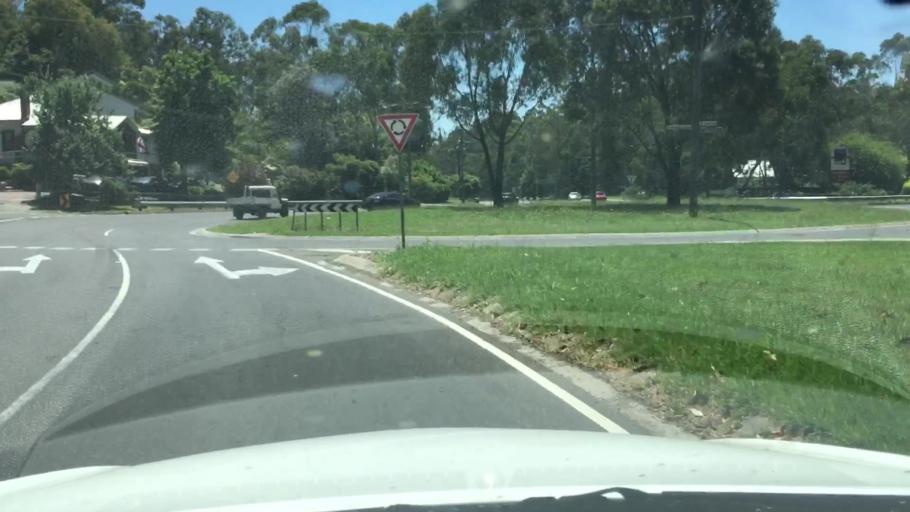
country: AU
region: Victoria
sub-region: Yarra Ranges
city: Kalorama
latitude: -37.7972
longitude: 145.3592
